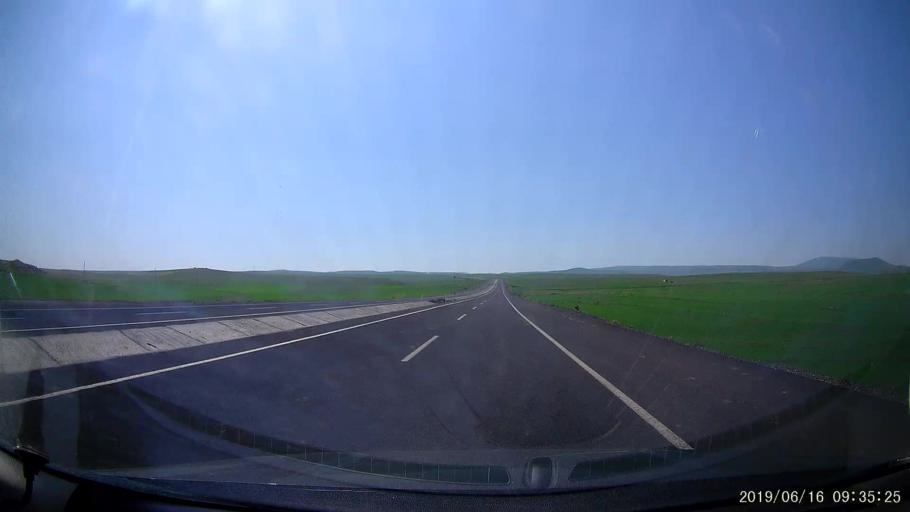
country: TR
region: Kars
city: Kars
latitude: 40.5723
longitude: 43.1556
